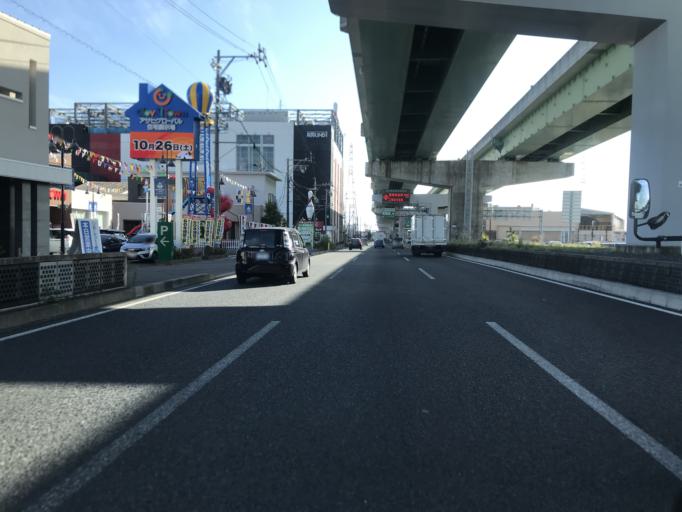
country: JP
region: Aichi
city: Iwakura
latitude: 35.2560
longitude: 136.8429
